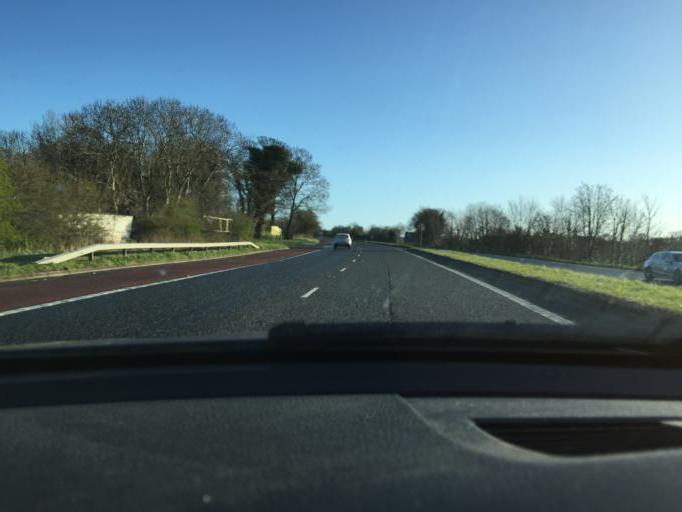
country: GB
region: Northern Ireland
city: Moira
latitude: 54.3893
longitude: -6.1785
